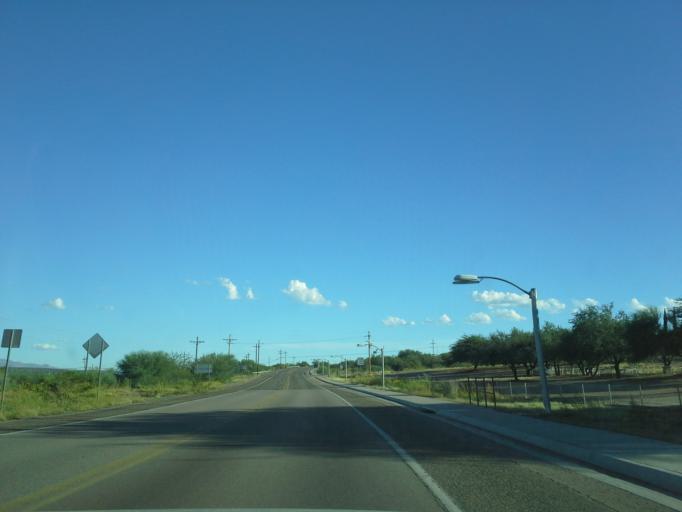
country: US
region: Arizona
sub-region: Pinal County
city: Mammoth
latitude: 32.7189
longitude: -110.6436
